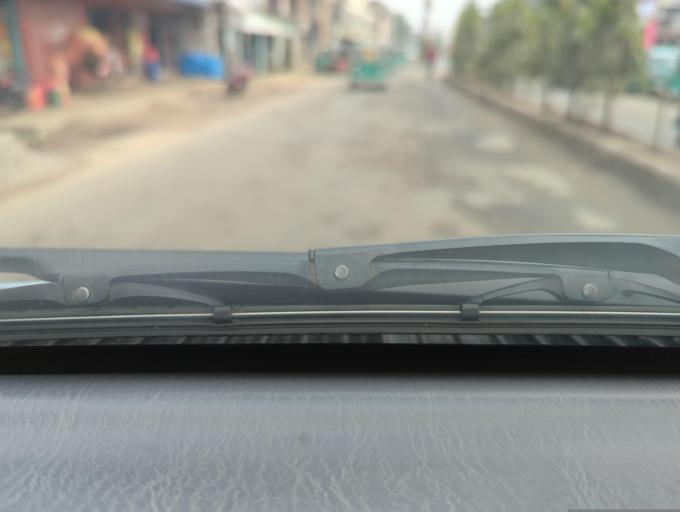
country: BD
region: Sylhet
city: Maulavi Bazar
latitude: 24.4899
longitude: 91.7547
